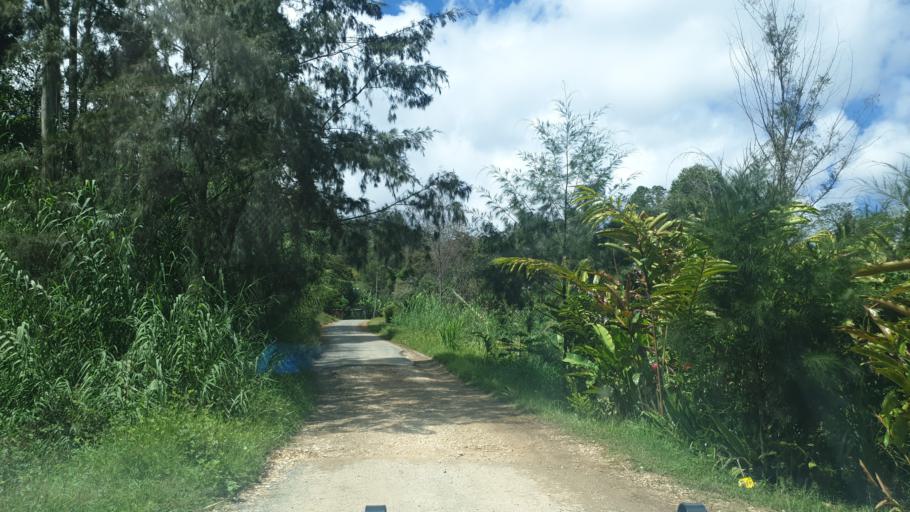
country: PG
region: Chimbu
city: Kundiawa
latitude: -6.1560
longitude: 145.1341
